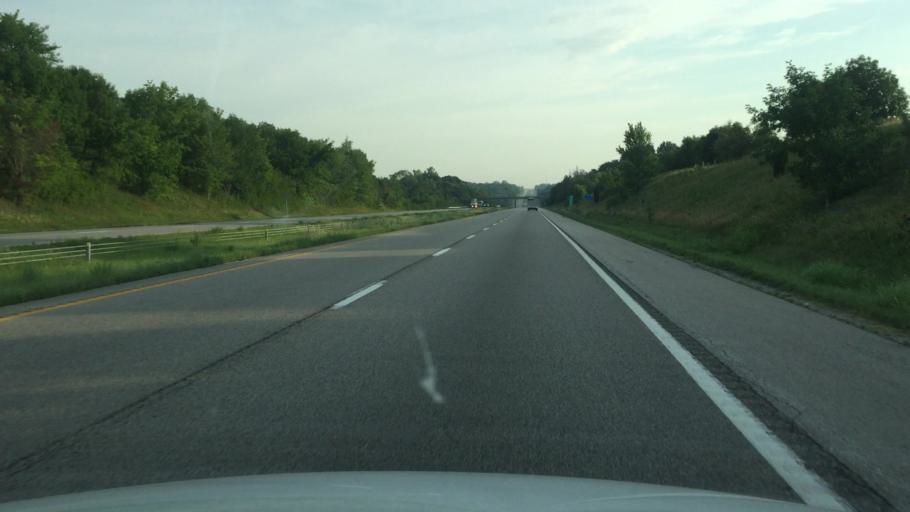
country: US
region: Missouri
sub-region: Buchanan County
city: Saint Joseph
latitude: 39.6462
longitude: -94.7878
